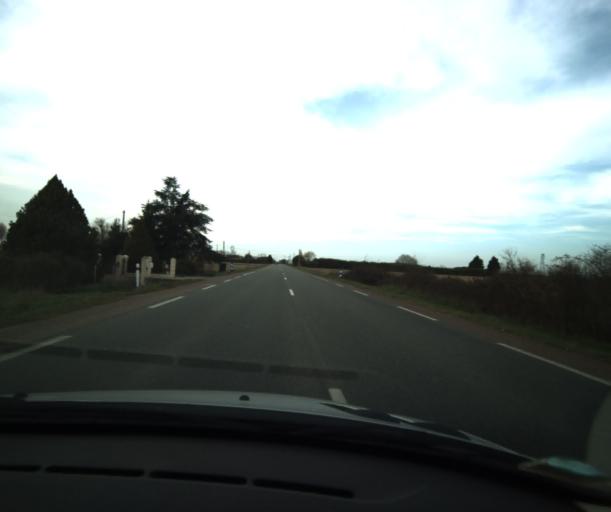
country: FR
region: Midi-Pyrenees
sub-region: Departement du Tarn-et-Garonne
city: Montech
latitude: 43.9718
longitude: 1.2041
